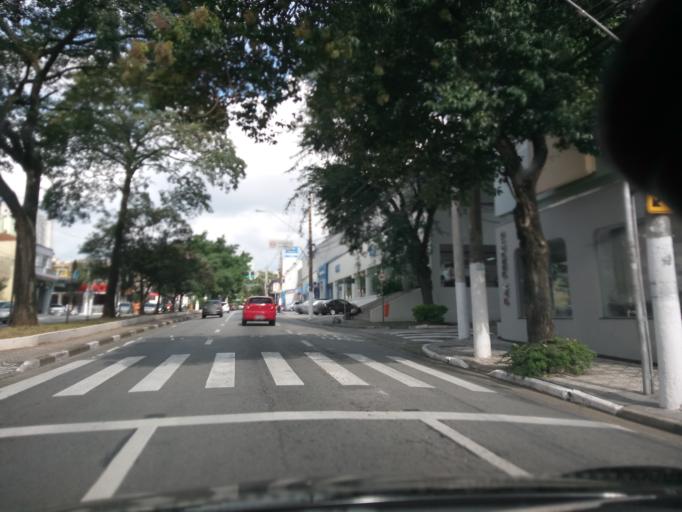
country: BR
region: Sao Paulo
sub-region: Sao Bernardo Do Campo
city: Sao Bernardo do Campo
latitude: -23.6667
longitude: -46.5687
